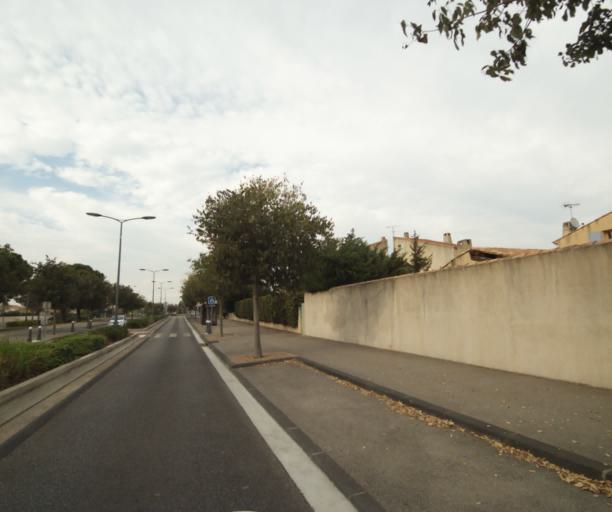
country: FR
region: Provence-Alpes-Cote d'Azur
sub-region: Departement des Bouches-du-Rhone
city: Marignane
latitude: 43.4176
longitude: 5.2033
